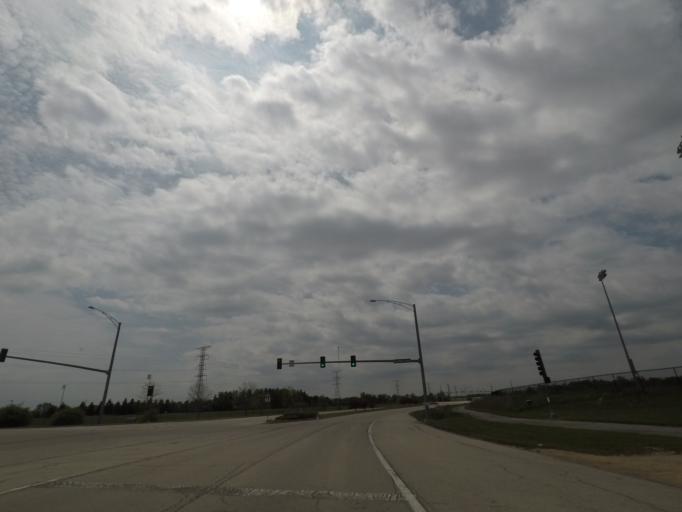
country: US
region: Illinois
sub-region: Winnebago County
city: Cherry Valley
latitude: 42.3221
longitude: -88.9483
